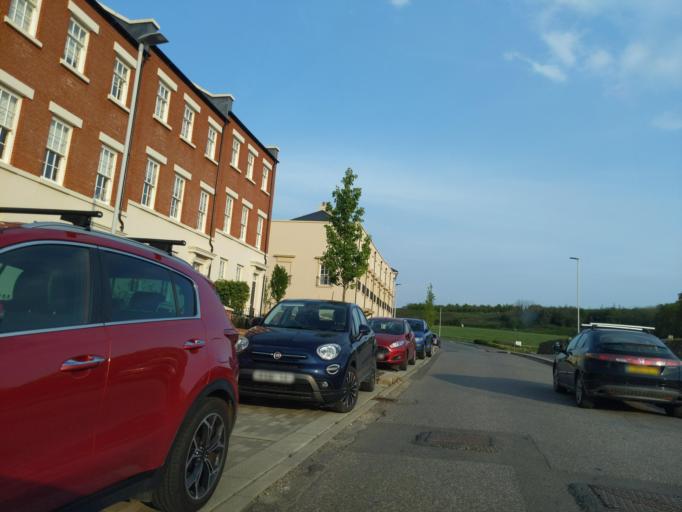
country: GB
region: England
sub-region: Devon
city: Plympton
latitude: 50.3631
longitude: -4.0512
